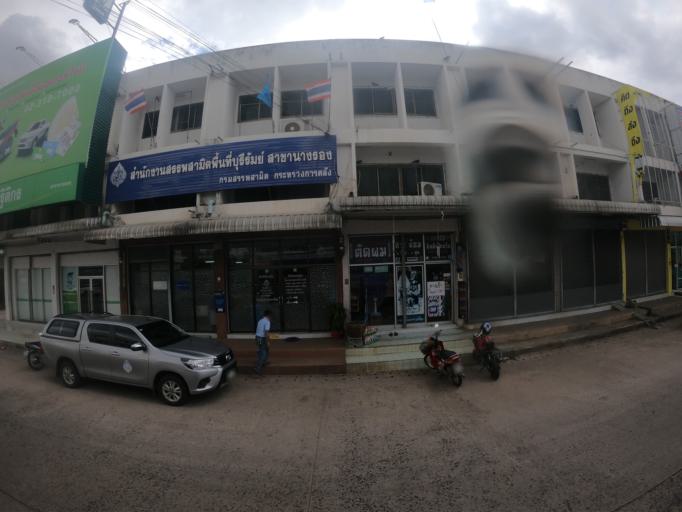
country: TH
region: Buriram
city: Nang Rong
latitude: 14.6332
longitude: 102.7813
